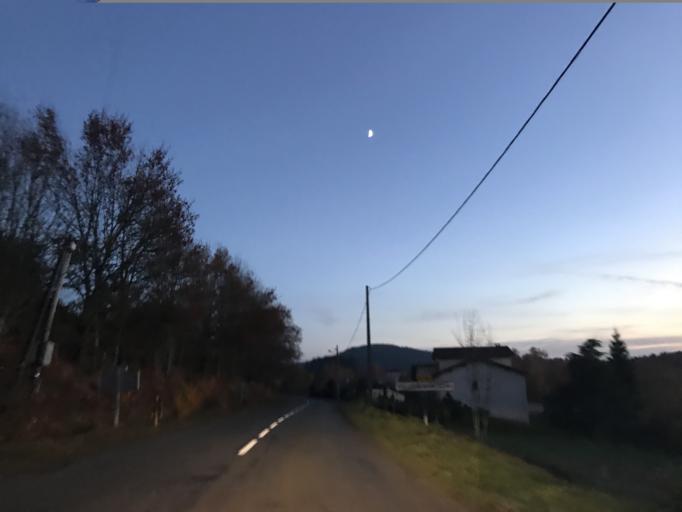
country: FR
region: Auvergne
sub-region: Departement du Puy-de-Dome
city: Celles-sur-Durolle
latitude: 45.7837
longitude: 3.6777
